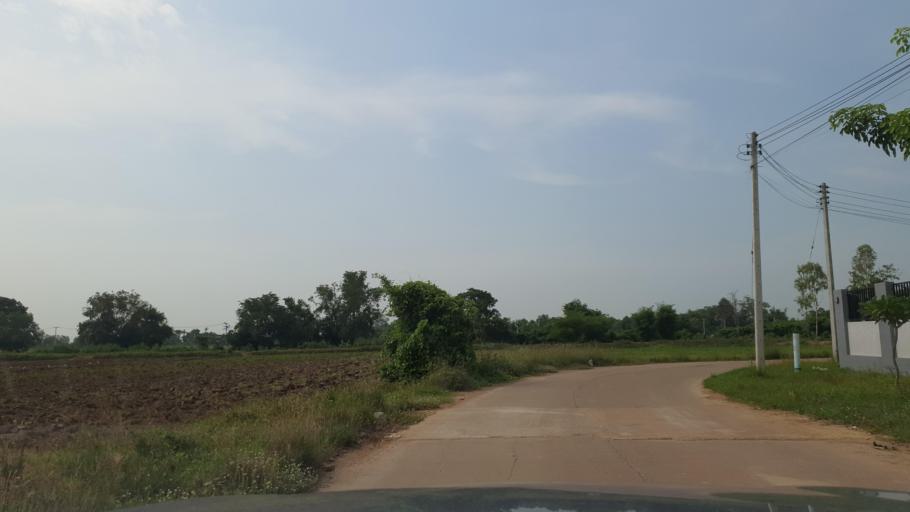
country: TH
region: Phitsanulok
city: Bang Rakam
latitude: 16.7980
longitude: 100.1637
